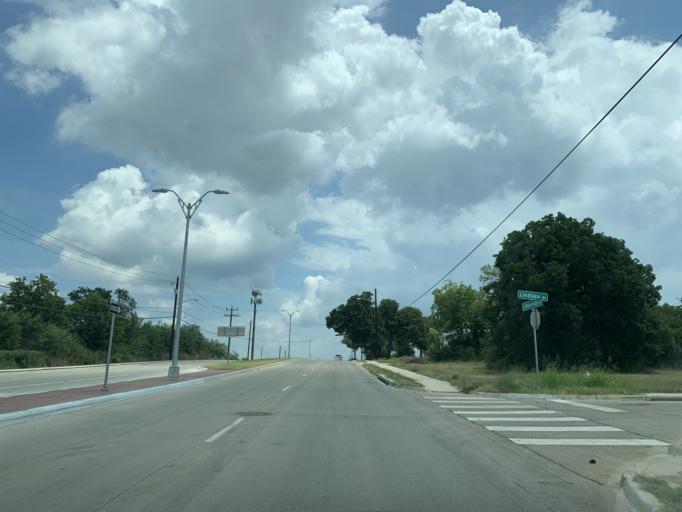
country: US
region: Texas
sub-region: Tarrant County
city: Forest Hill
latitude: 32.7311
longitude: -97.2529
